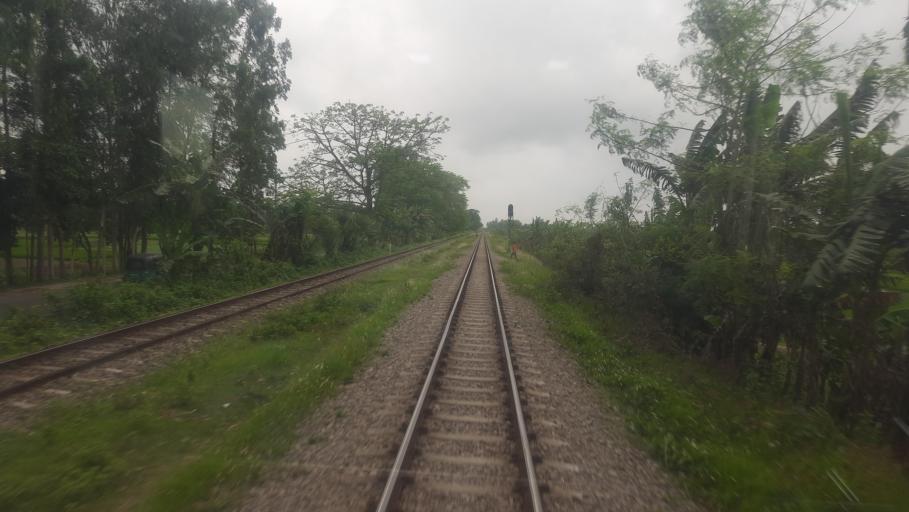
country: BD
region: Dhaka
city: Narsingdi
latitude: 23.9472
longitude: 90.7902
